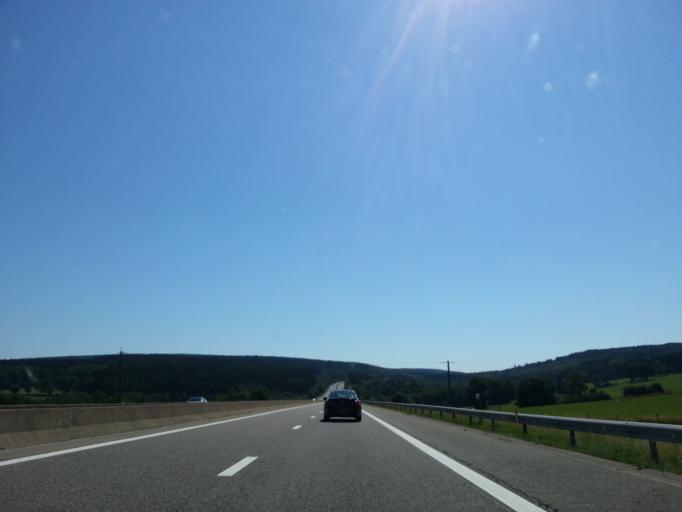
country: BE
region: Wallonia
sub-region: Province de Liege
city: Malmedy
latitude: 50.3595
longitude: 6.0473
